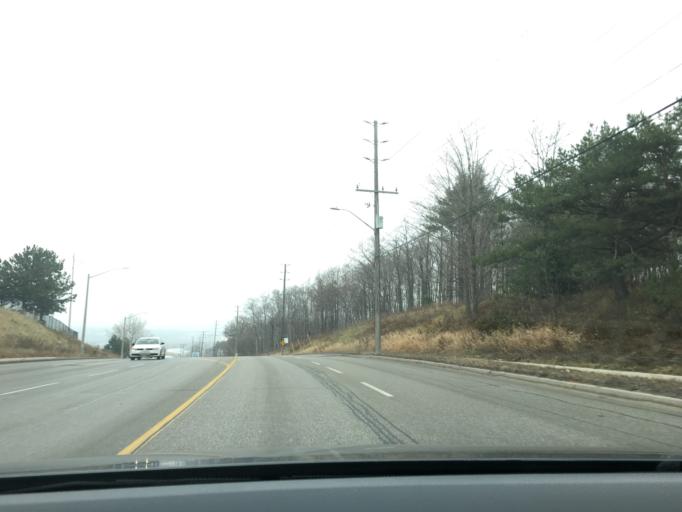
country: CA
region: Ontario
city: Barrie
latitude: 44.3516
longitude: -79.6999
